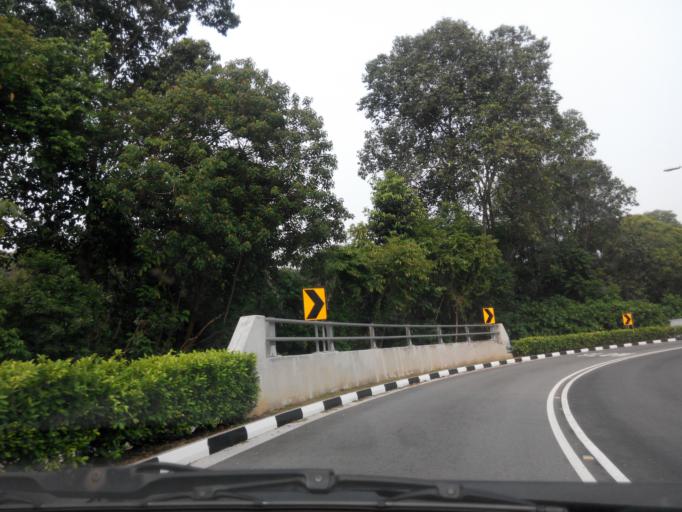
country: SG
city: Singapore
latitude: 1.2872
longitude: 103.7905
